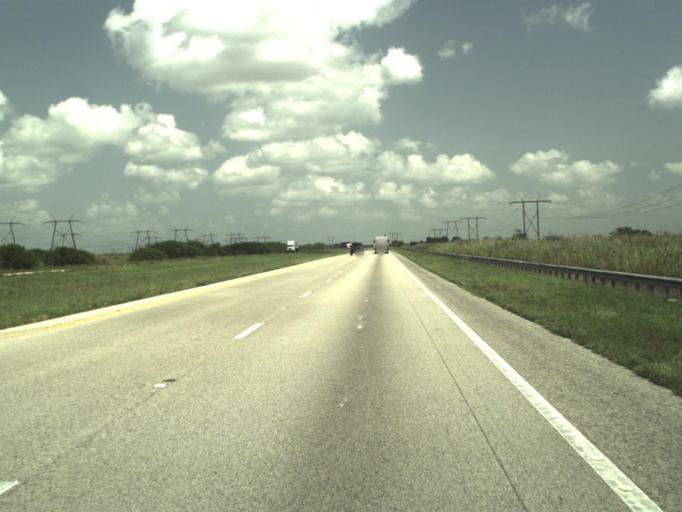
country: US
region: Florida
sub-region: Broward County
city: Weston
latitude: 26.2186
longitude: -80.4578
